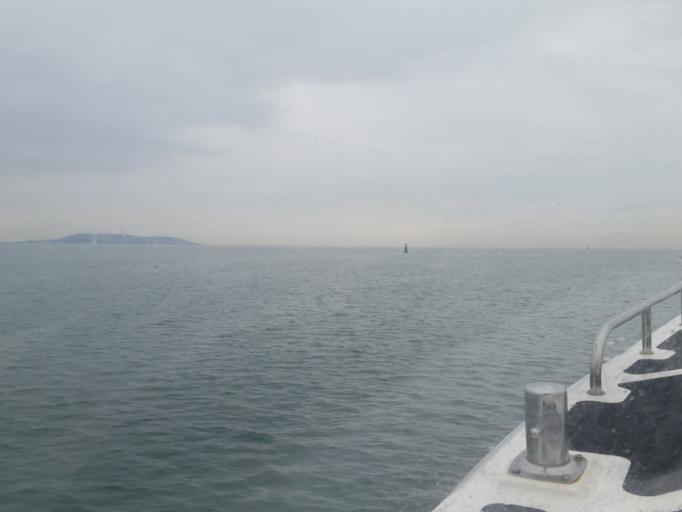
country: IE
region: Leinster
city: Malahide
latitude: 53.4511
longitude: -6.1288
